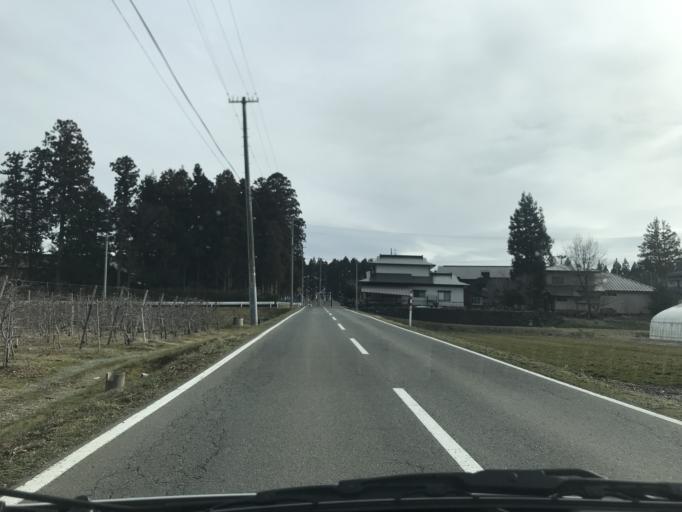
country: JP
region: Iwate
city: Hanamaki
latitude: 39.3741
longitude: 141.0701
